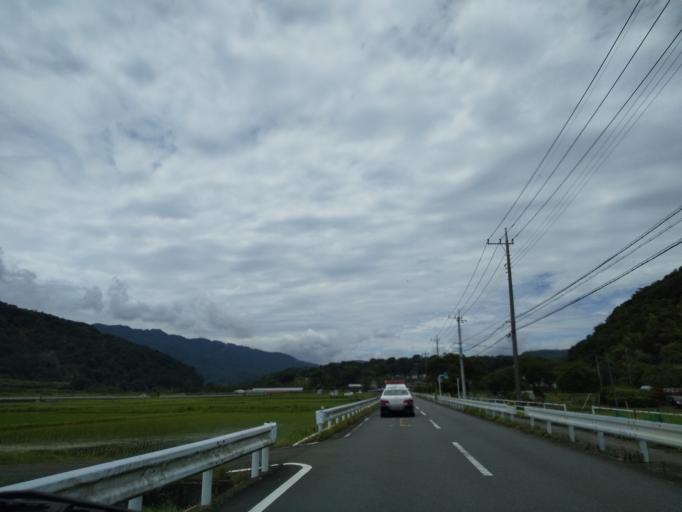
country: JP
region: Kanagawa
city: Zama
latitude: 35.5267
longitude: 139.3173
